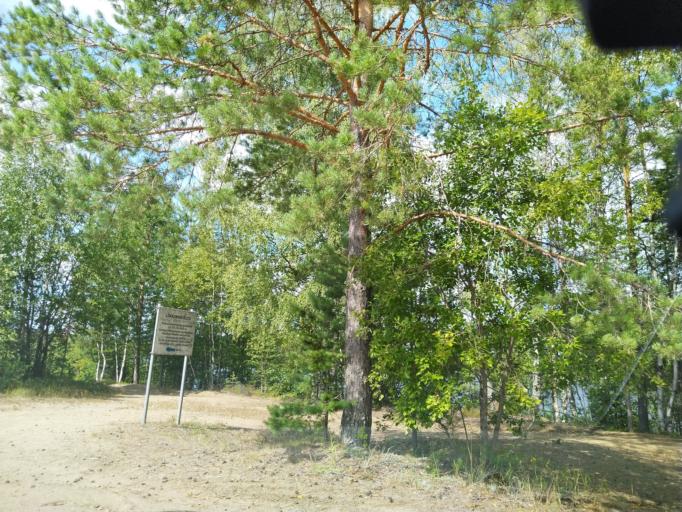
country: FI
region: Uusimaa
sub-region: Helsinki
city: Kaerkoelae
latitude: 60.7513
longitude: 24.0997
